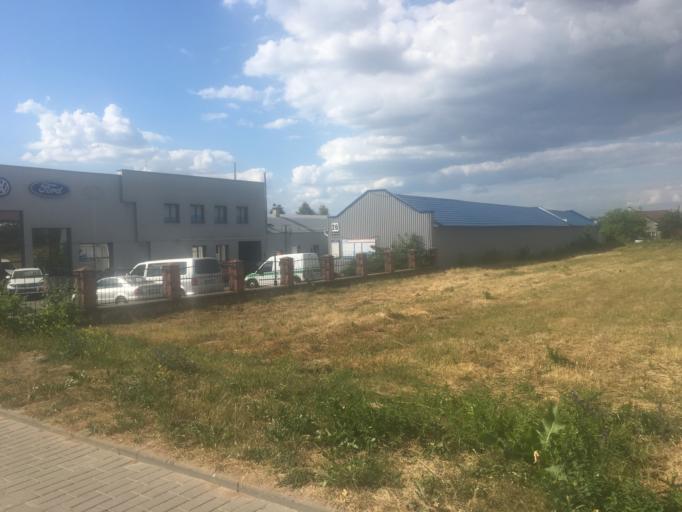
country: BY
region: Grodnenskaya
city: Hrodna
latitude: 53.6481
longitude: 23.8124
